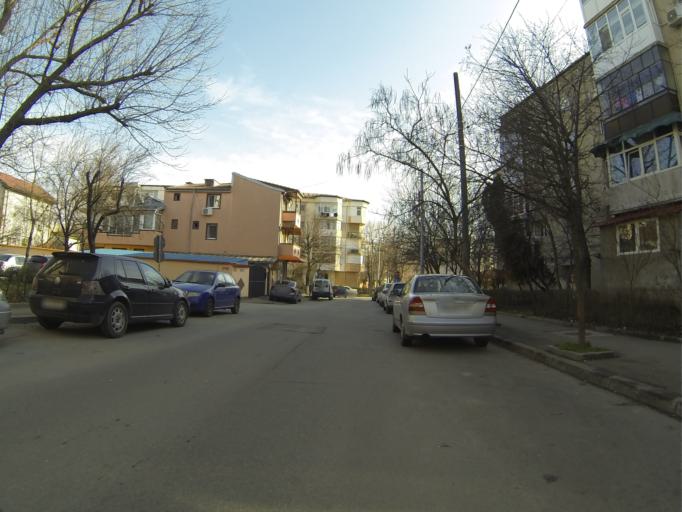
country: RO
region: Dolj
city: Craiova
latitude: 44.3062
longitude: 23.8146
